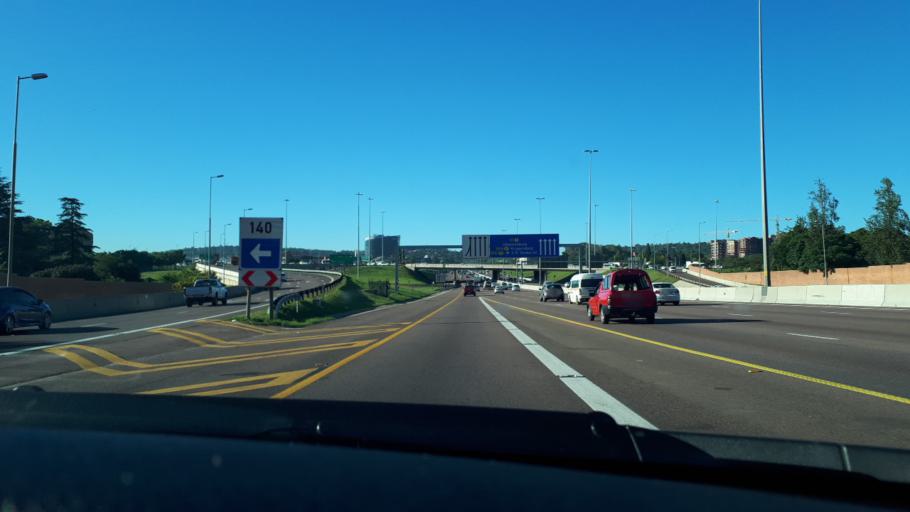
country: ZA
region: Gauteng
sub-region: City of Tshwane Metropolitan Municipality
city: Pretoria
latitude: -25.7752
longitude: 28.2729
